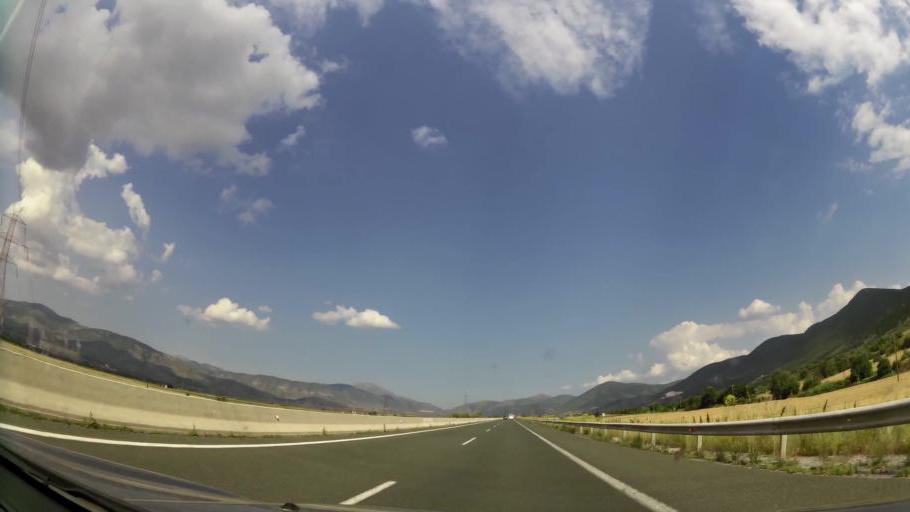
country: GR
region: West Macedonia
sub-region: Nomos Kozanis
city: Akrini
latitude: 40.3688
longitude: 21.8995
